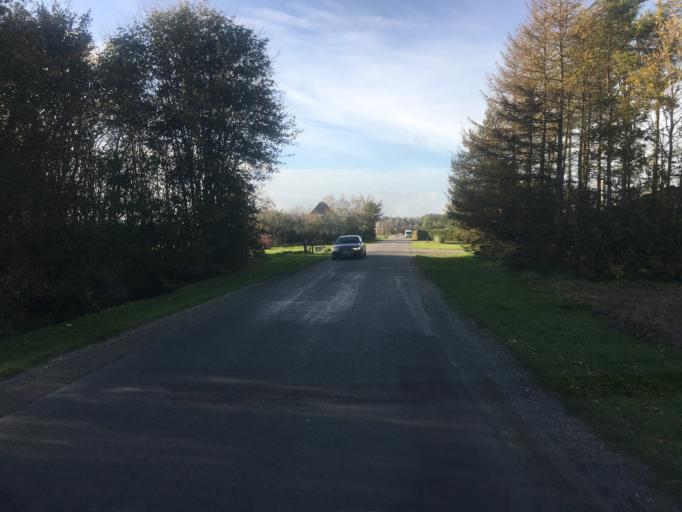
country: DK
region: South Denmark
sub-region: Tonder Kommune
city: Logumkloster
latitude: 55.0740
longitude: 8.9396
